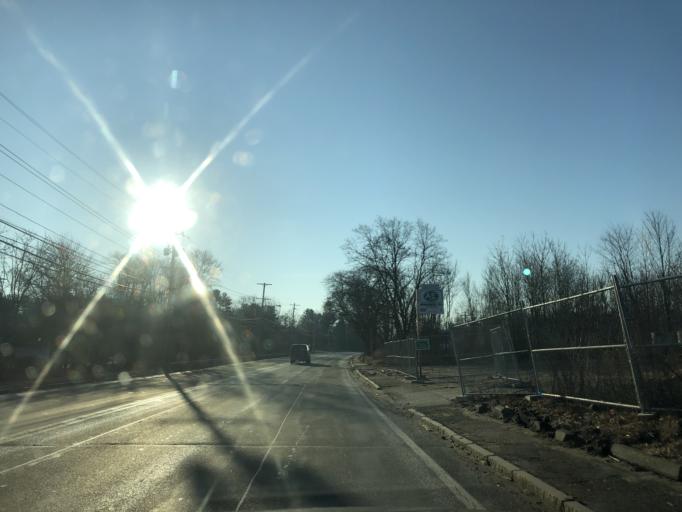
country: US
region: Massachusetts
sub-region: Norfolk County
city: Avon
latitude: 42.1213
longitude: -71.0329
